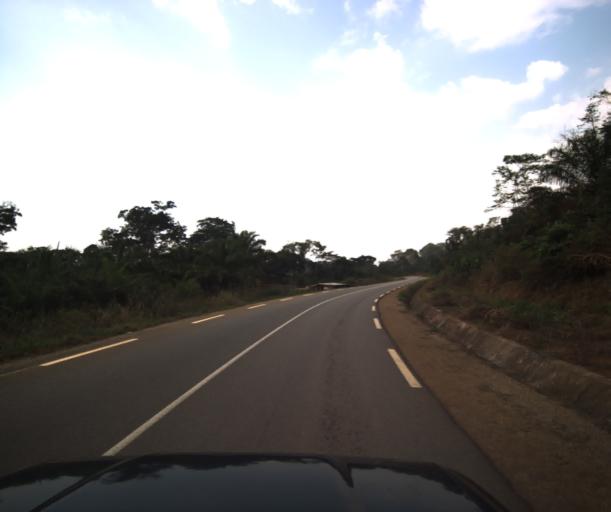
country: CM
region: Centre
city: Mbankomo
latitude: 3.6597
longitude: 11.3410
